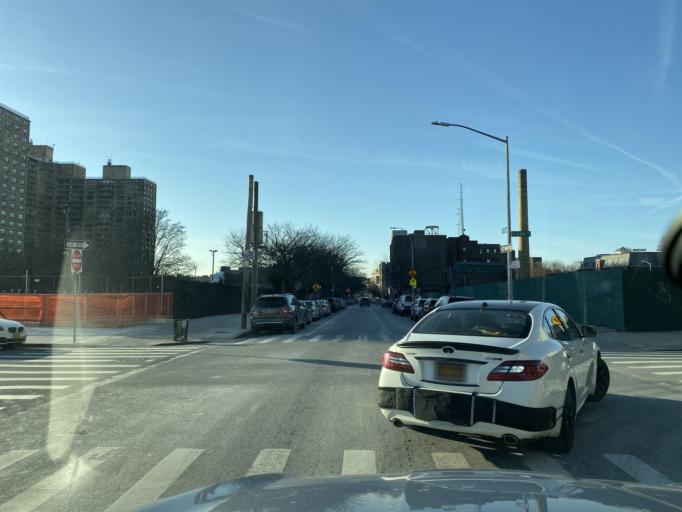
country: US
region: New York
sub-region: Kings County
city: Brooklyn
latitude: 40.6673
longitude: -73.9592
